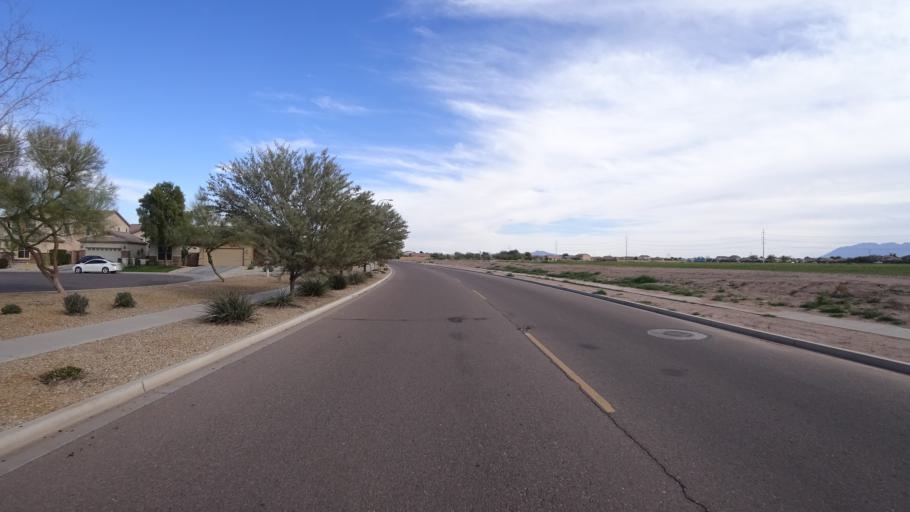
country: US
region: Arizona
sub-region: Maricopa County
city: Tolleson
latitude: 33.4103
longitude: -112.2784
